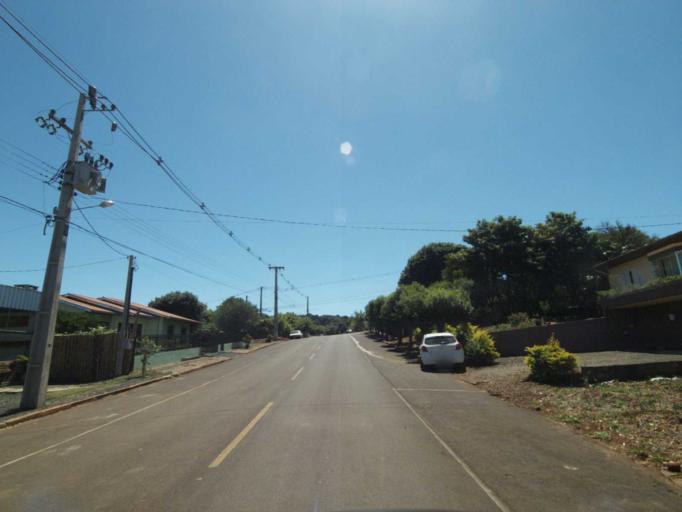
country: BR
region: Parana
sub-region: Coronel Vivida
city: Coronel Vivida
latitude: -25.9665
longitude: -52.8177
